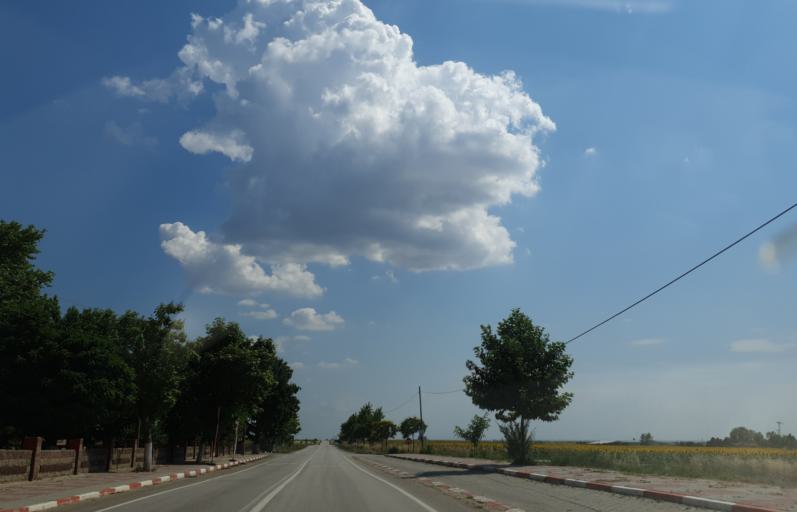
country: TR
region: Kirklareli
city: Buyukkaristiran
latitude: 41.4346
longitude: 27.5835
